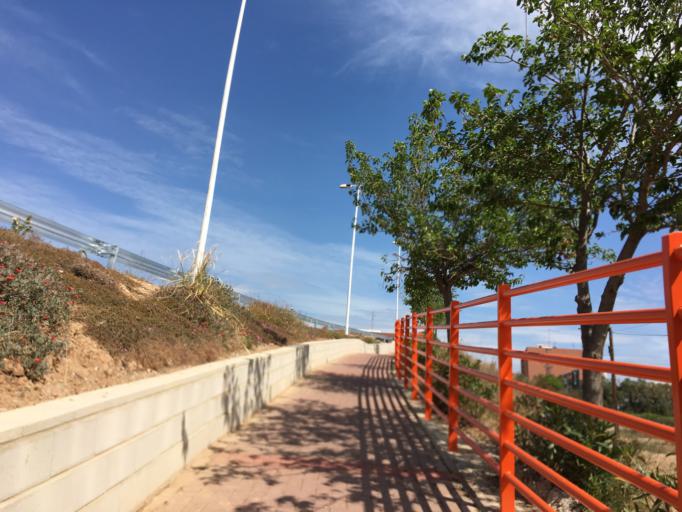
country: ES
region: Valencia
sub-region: Provincia de Valencia
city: Paterna
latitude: 39.4952
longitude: -0.4189
